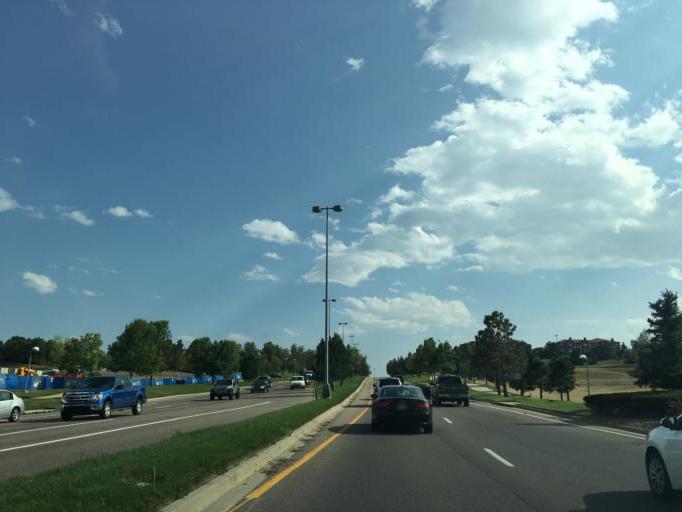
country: US
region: Colorado
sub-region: Broomfield County
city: Broomfield
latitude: 39.9284
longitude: -105.1279
